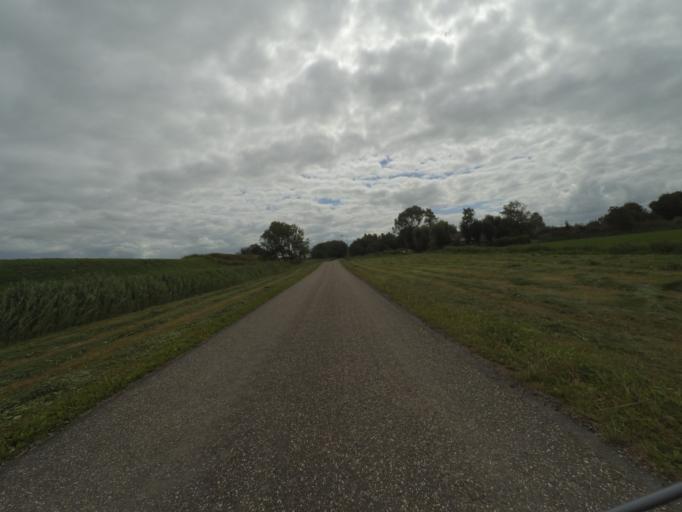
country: NL
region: Friesland
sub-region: Gemeente Dongeradeel
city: Anjum
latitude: 53.3324
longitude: 6.1542
